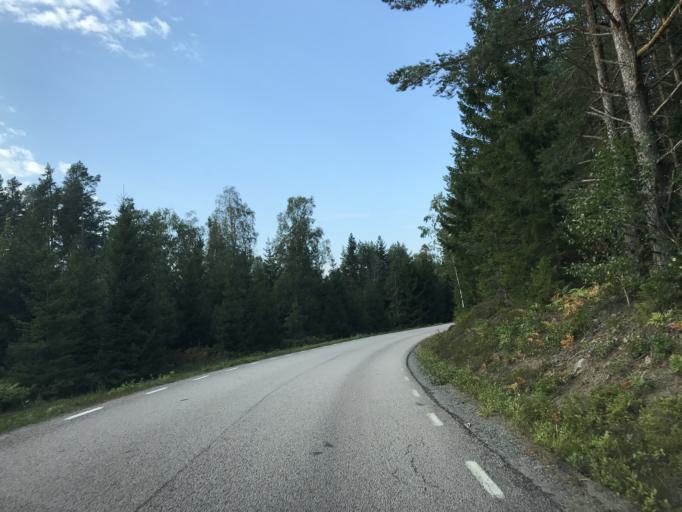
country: SE
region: Stockholm
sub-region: Norrtalje Kommun
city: Bjorko
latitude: 59.8829
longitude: 18.9795
